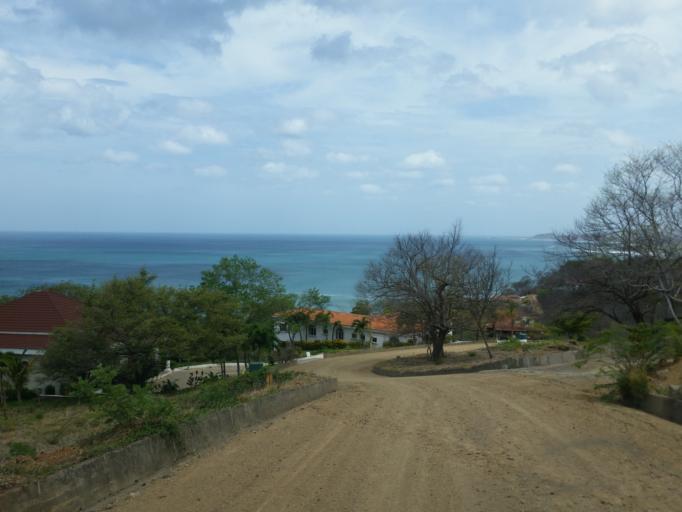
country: NI
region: Rivas
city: Tola
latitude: 11.4337
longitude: -86.0800
